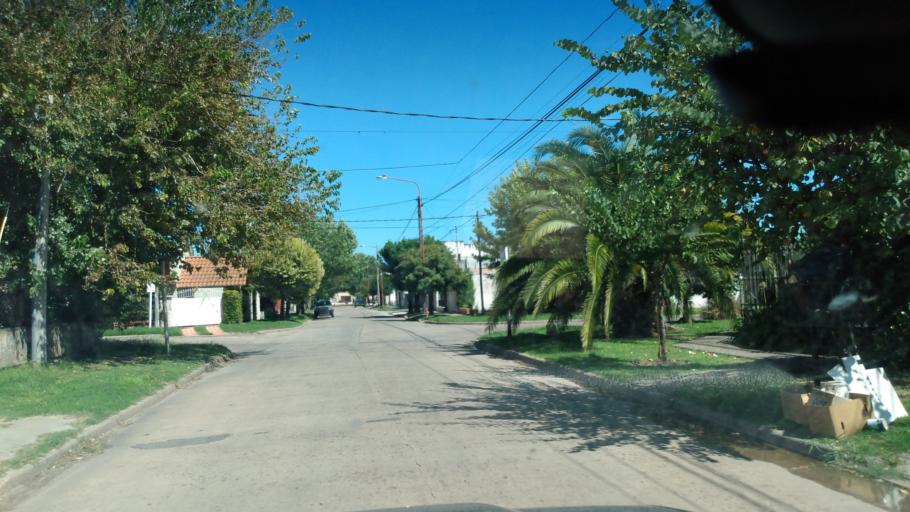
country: AR
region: Buenos Aires
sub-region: Partido de Lujan
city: Lujan
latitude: -34.5780
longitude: -59.1104
